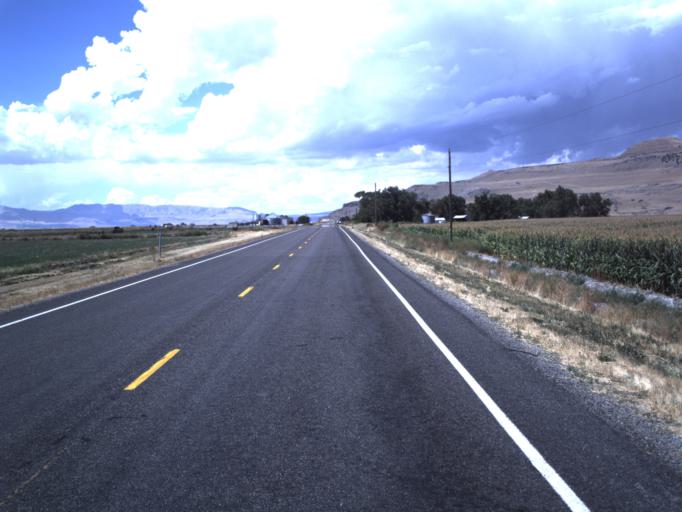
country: US
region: Utah
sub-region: Box Elder County
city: Elwood
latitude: 41.5697
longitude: -112.2000
